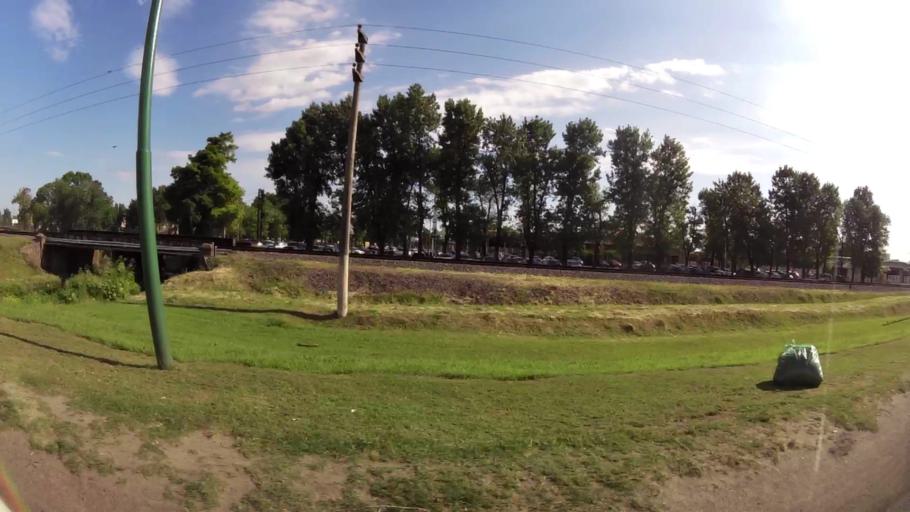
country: AR
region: Buenos Aires
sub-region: Partido de Merlo
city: Merlo
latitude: -34.6616
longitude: -58.7457
